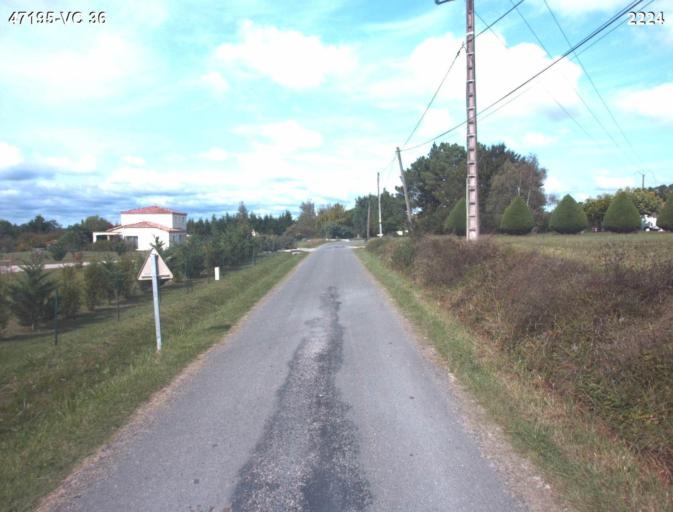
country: FR
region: Aquitaine
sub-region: Departement du Lot-et-Garonne
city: Nerac
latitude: 44.1266
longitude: 0.3257
